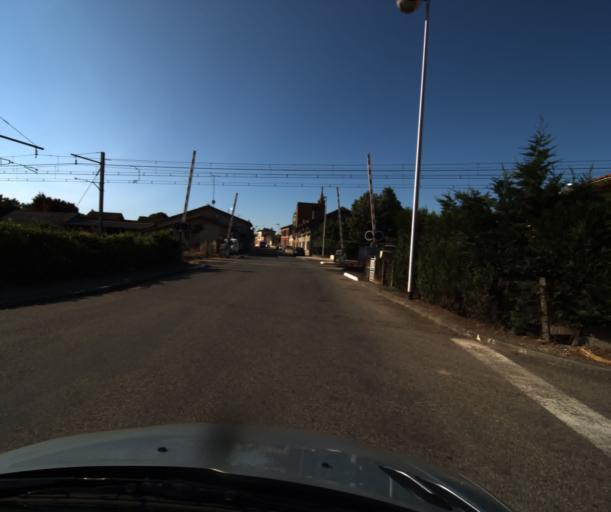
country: FR
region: Midi-Pyrenees
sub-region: Departement du Tarn-et-Garonne
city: Saint-Porquier
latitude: 44.0357
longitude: 1.2169
